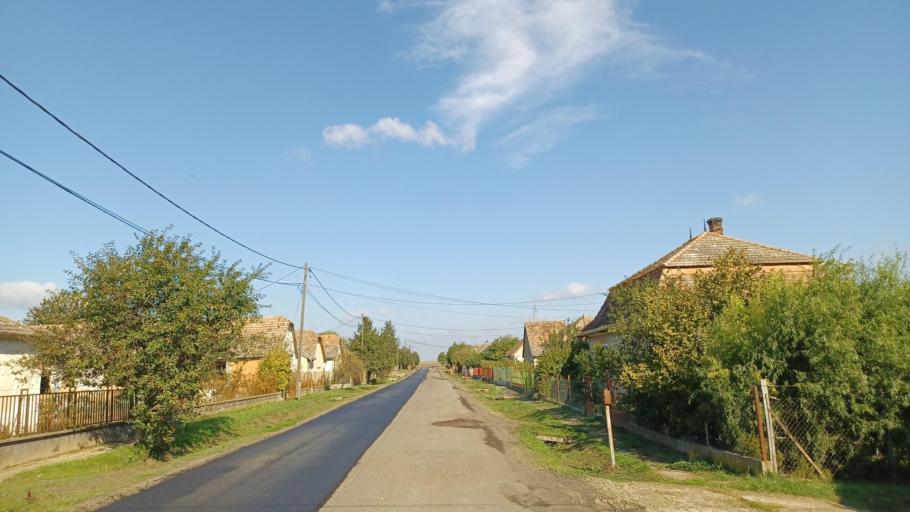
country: HU
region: Tolna
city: Nagydorog
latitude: 46.6045
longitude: 18.5939
